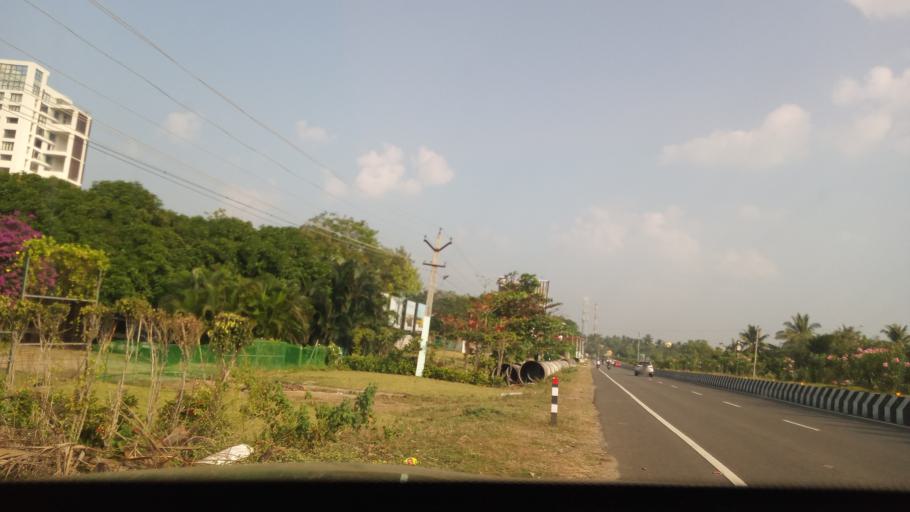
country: IN
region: Tamil Nadu
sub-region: Kancheepuram
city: Injambakkam
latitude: 12.7740
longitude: 80.2489
